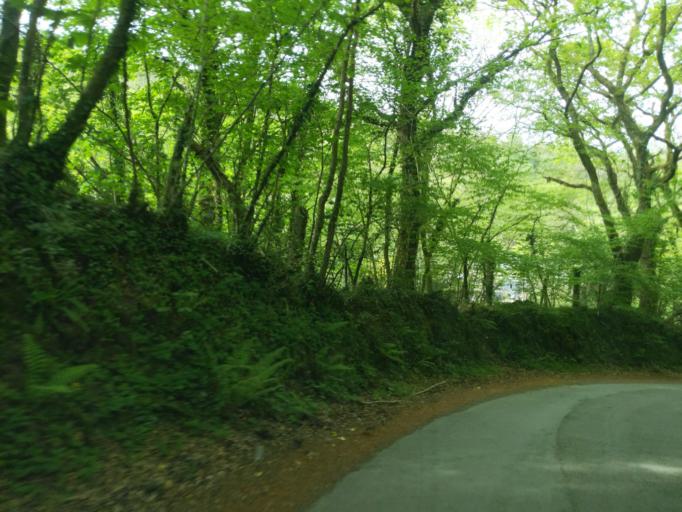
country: GB
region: England
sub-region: Devon
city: Plympton
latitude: 50.4370
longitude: -4.0764
